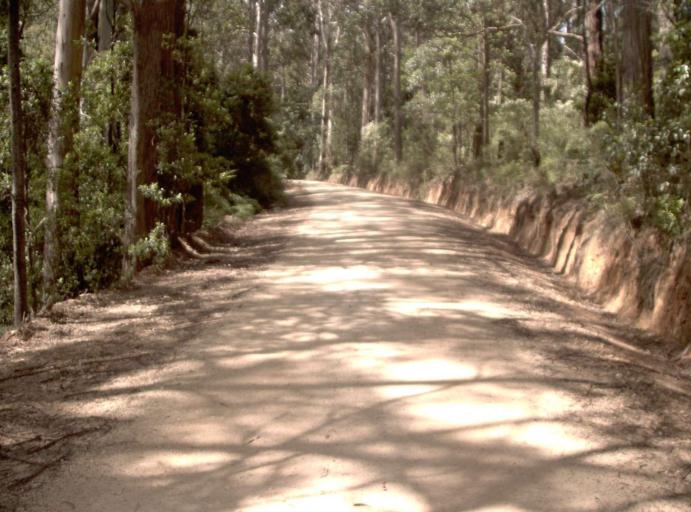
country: AU
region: Victoria
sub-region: East Gippsland
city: Lakes Entrance
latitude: -37.5845
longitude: 148.7260
